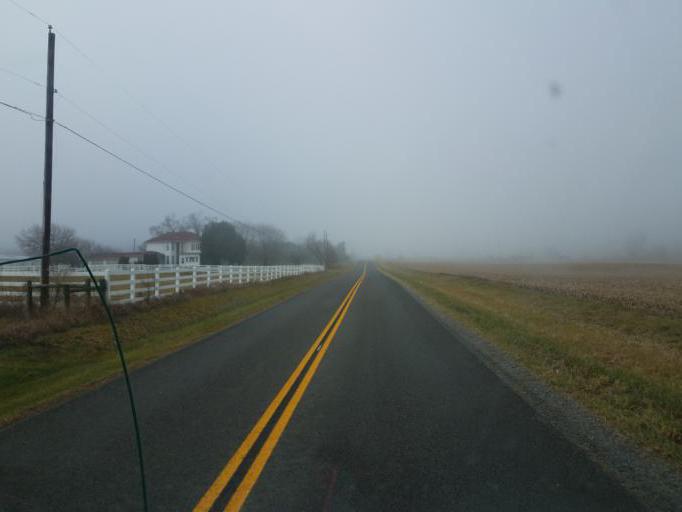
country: US
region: Ohio
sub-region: Champaign County
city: North Lewisburg
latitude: 40.3035
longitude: -83.6067
